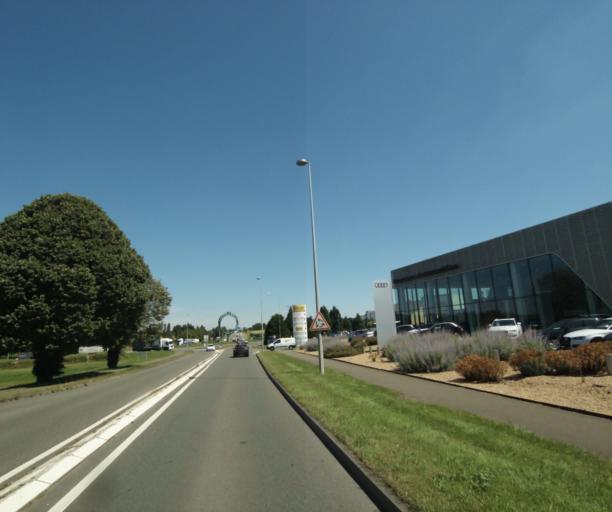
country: FR
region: Pays de la Loire
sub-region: Departement de la Mayenne
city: Laval
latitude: 48.0902
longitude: -0.7495
